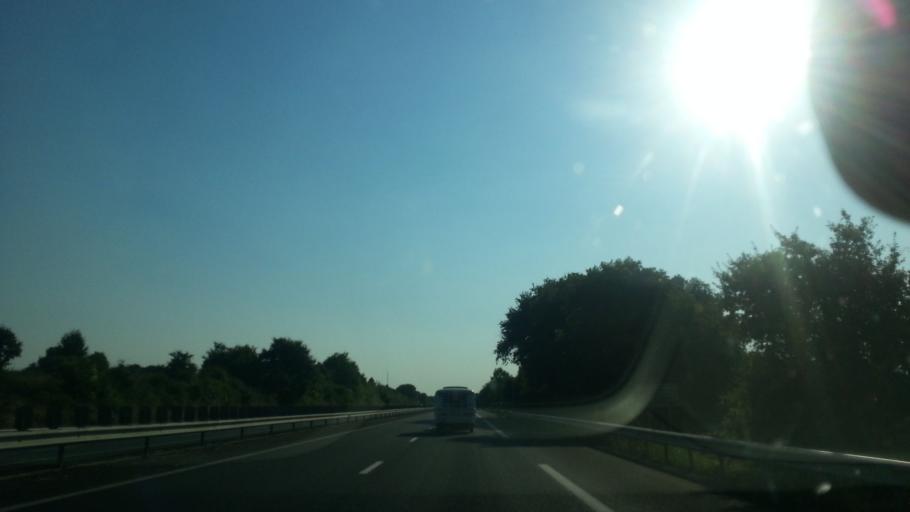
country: FR
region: Poitou-Charentes
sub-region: Departement de la Vienne
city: Rouille
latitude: 46.4714
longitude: 0.0398
